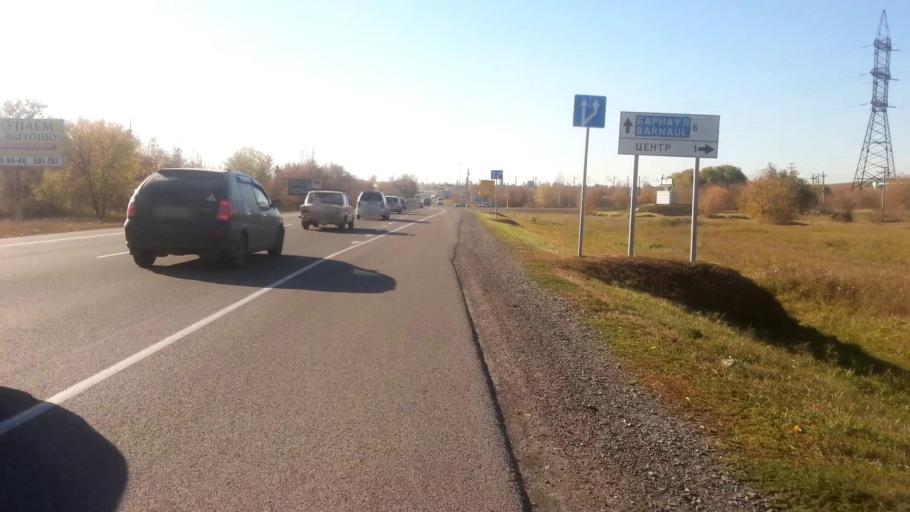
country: RU
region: Altai Krai
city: Novoaltaysk
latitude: 53.3741
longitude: 83.9380
